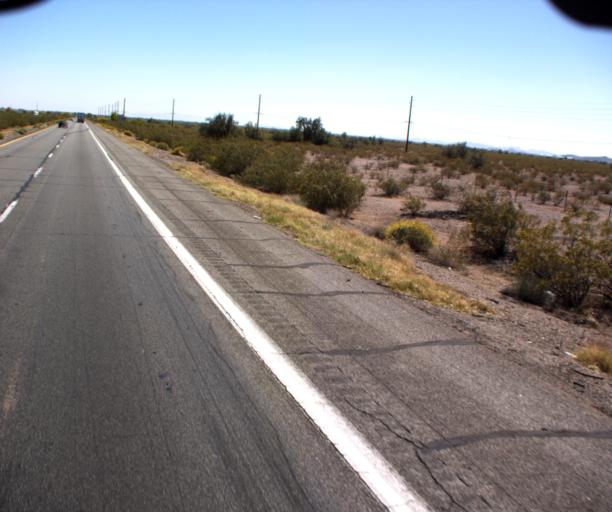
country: US
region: Arizona
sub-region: Maricopa County
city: Buckeye
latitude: 33.4951
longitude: -112.9275
